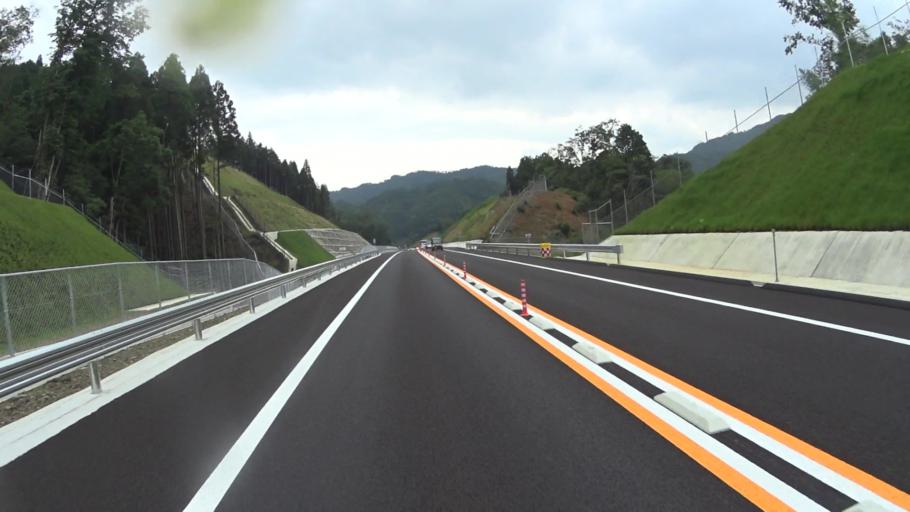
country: JP
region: Kyoto
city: Ayabe
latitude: 35.2243
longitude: 135.3441
